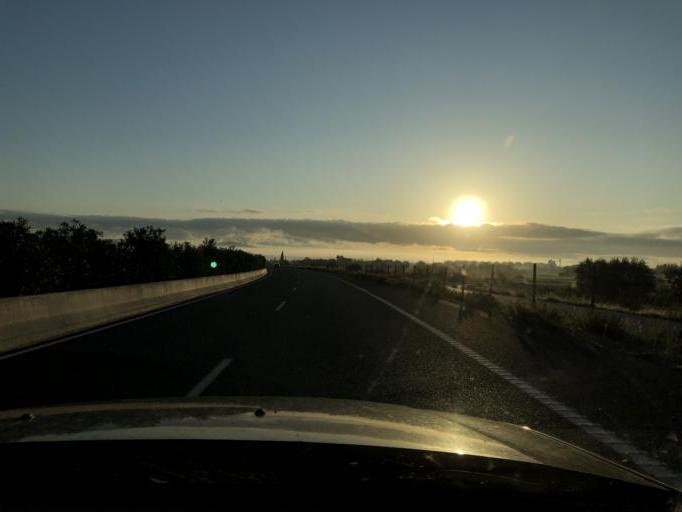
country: ES
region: Balearic Islands
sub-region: Illes Balears
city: Montuiri
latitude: 39.5621
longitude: 2.9623
